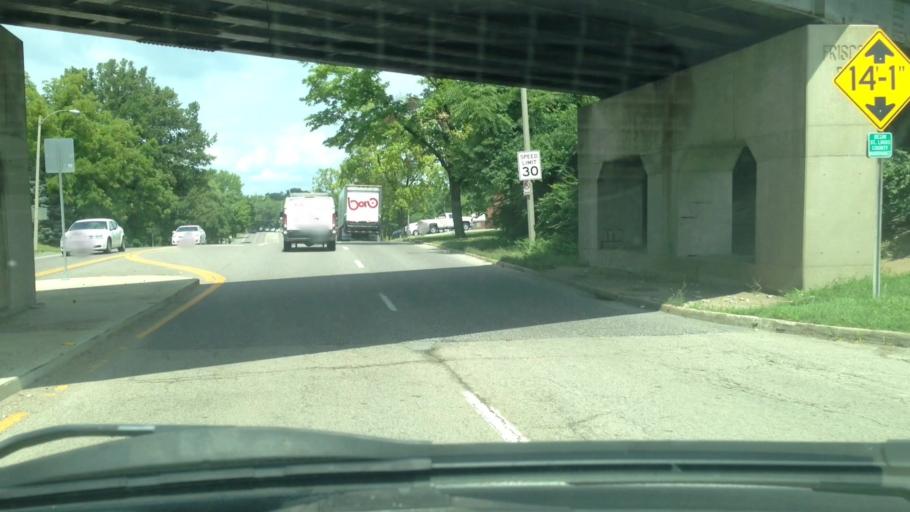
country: US
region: Missouri
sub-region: Saint Louis County
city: Shrewsbury
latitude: 38.5963
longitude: -90.3262
